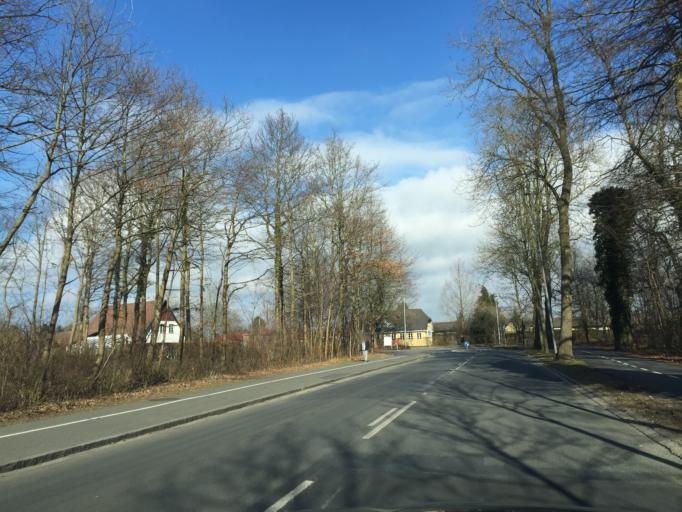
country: DK
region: South Denmark
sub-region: Odense Kommune
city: Neder Holluf
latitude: 55.3840
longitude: 10.4401
